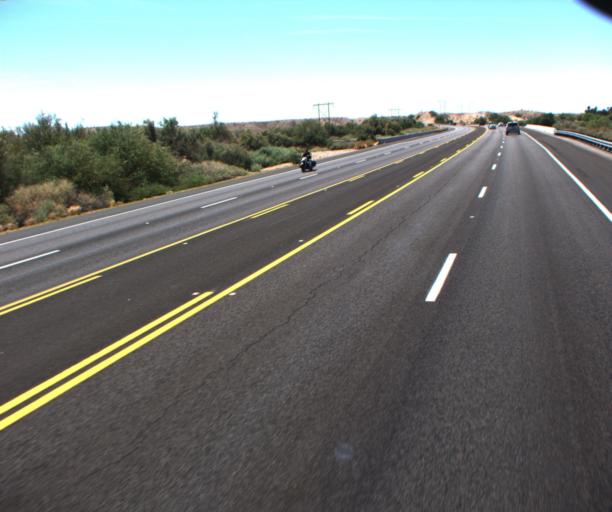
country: US
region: Arizona
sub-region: La Paz County
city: Cienega Springs
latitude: 34.1768
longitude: -114.2424
